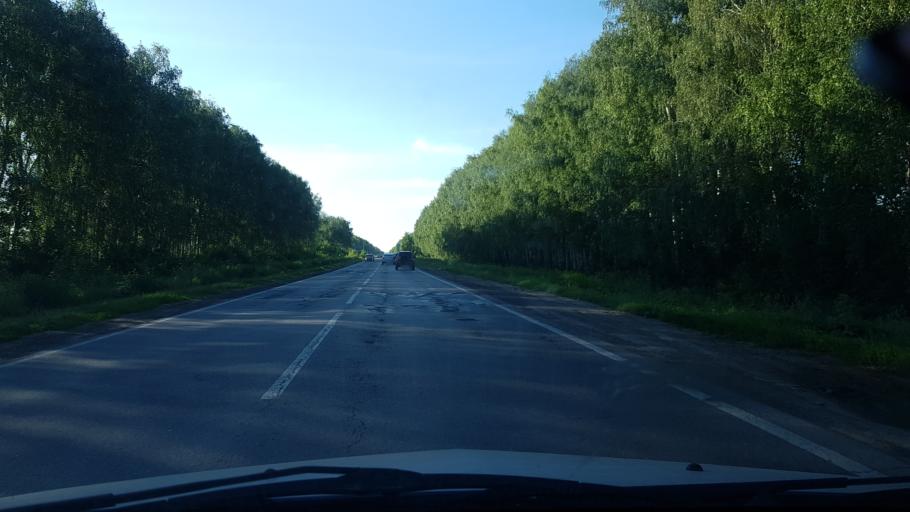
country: RU
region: Samara
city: Tol'yatti
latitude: 53.5932
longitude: 49.3276
